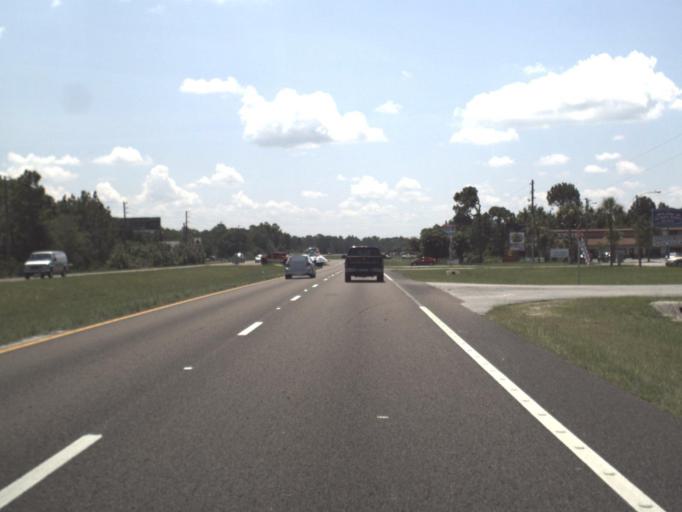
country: US
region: Florida
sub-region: Citrus County
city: Homosassa Springs
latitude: 28.7844
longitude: -82.5612
